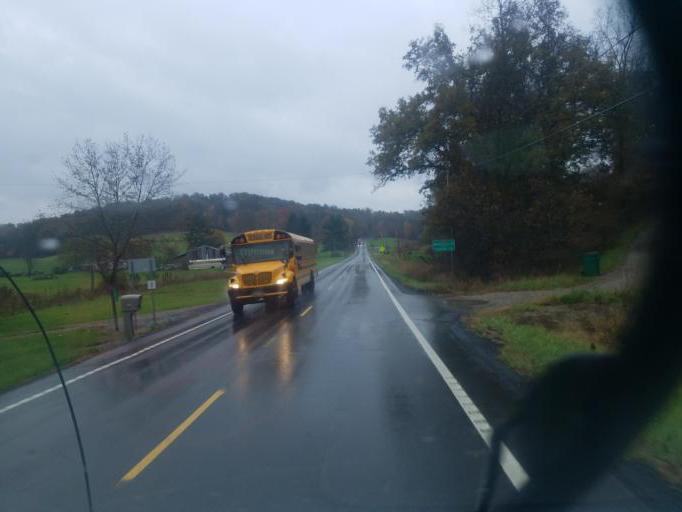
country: US
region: Ohio
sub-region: Muskingum County
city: Frazeysburg
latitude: 40.1224
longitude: -82.1896
